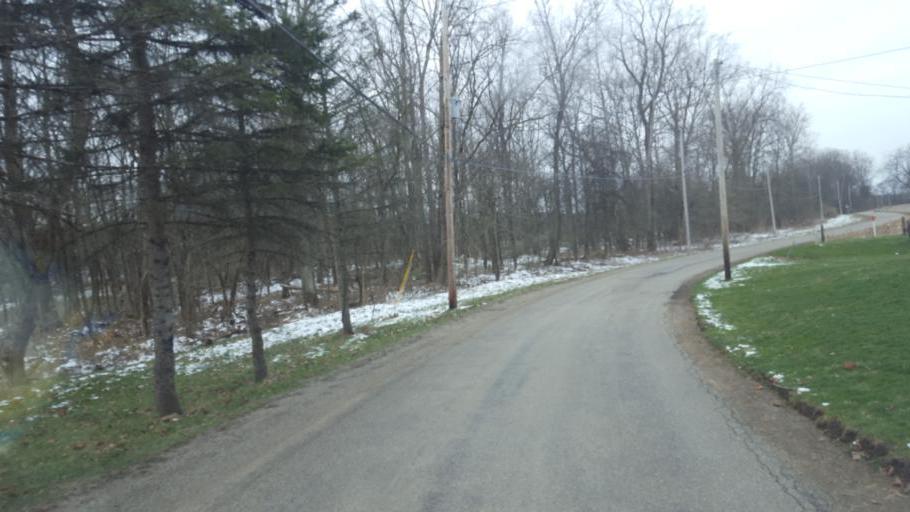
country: US
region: Ohio
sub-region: Sandusky County
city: Bellville
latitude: 40.5984
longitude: -82.4451
